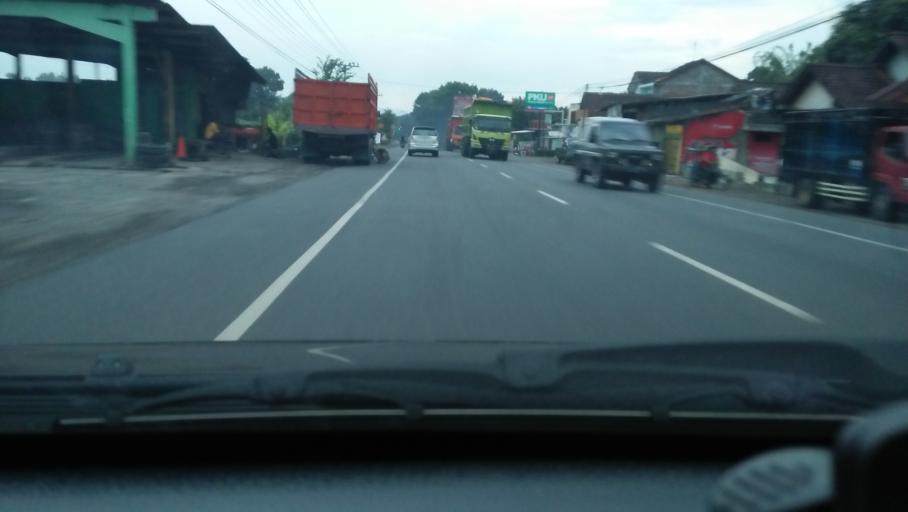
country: ID
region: Central Java
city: Magelang
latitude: -7.4039
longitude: 110.2400
